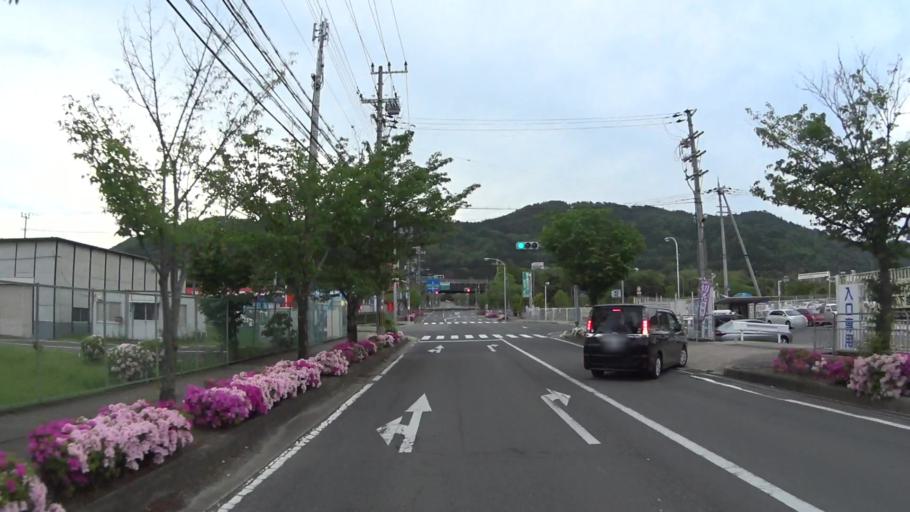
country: JP
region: Kyoto
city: Kameoka
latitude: 35.0310
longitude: 135.5473
